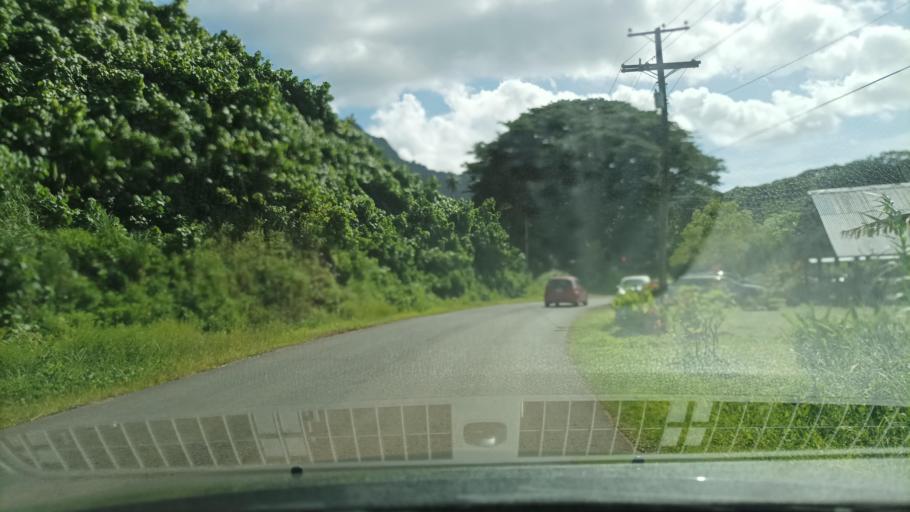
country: FM
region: Kosrae
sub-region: Lelu Municipality
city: Tofol
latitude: 5.3250
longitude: 163.0097
